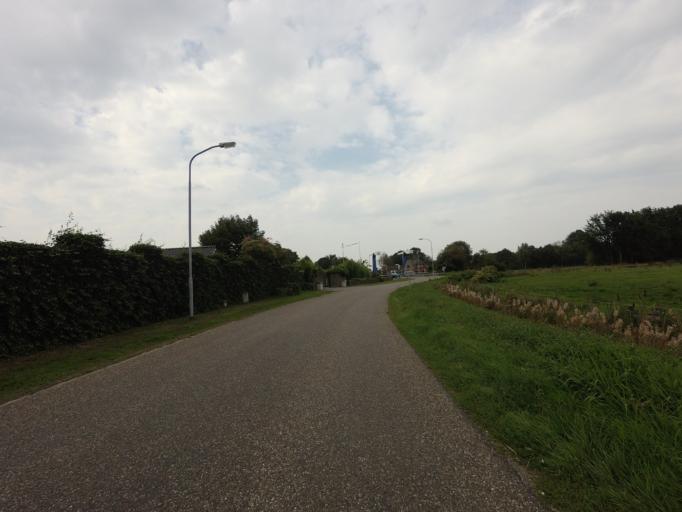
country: NL
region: Drenthe
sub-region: Gemeente Tynaarlo
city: Tynaarlo
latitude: 53.0367
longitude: 6.6077
